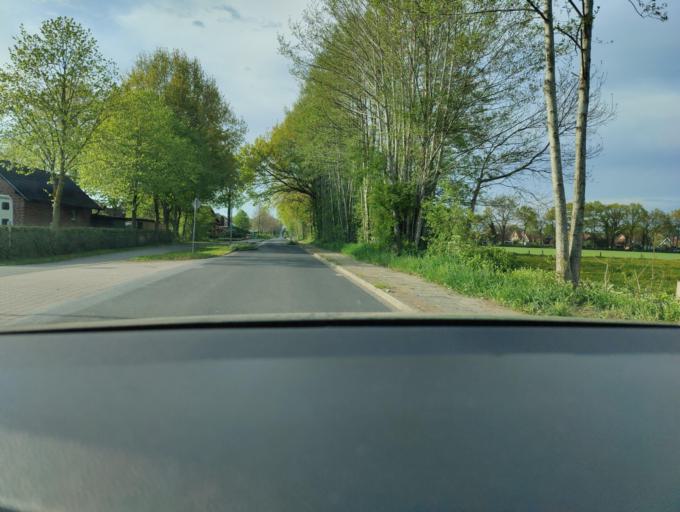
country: DE
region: Lower Saxony
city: Wietmarschen
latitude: 52.5085
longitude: 7.1383
